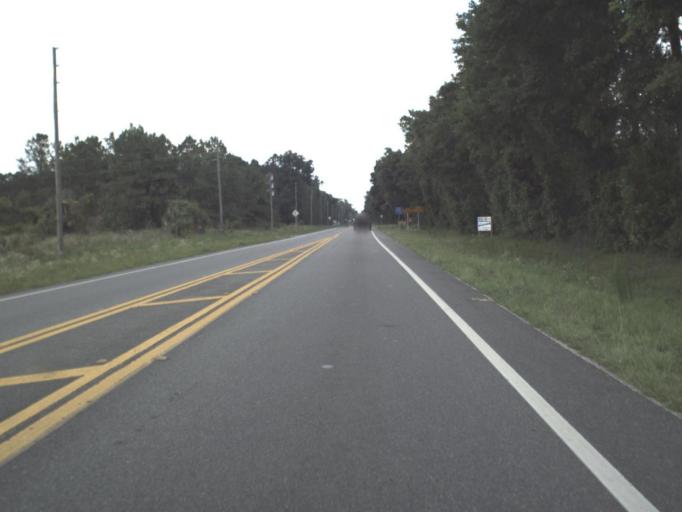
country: US
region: Florida
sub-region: Levy County
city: Manatee Road
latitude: 29.5954
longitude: -82.9234
